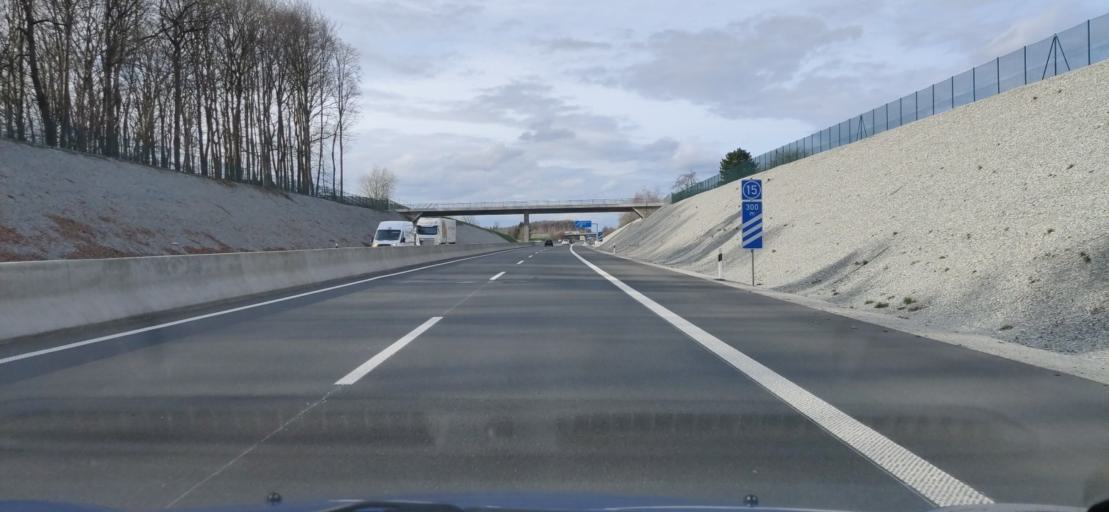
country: DE
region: North Rhine-Westphalia
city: Borgholzhausen
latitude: 52.0729
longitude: 8.2536
